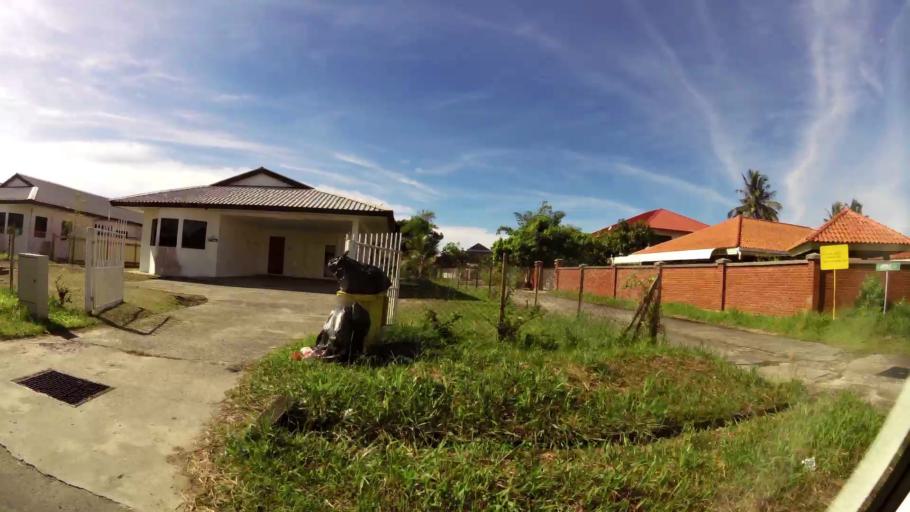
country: BN
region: Belait
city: Kuala Belait
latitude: 4.5858
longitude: 114.2153
